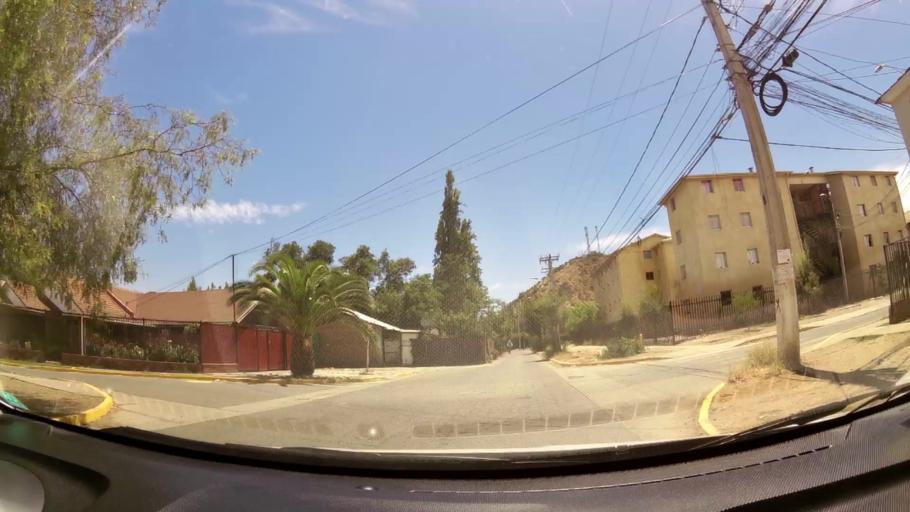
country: CL
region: O'Higgins
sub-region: Provincia de Cachapoal
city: Graneros
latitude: -34.0583
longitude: -70.7268
